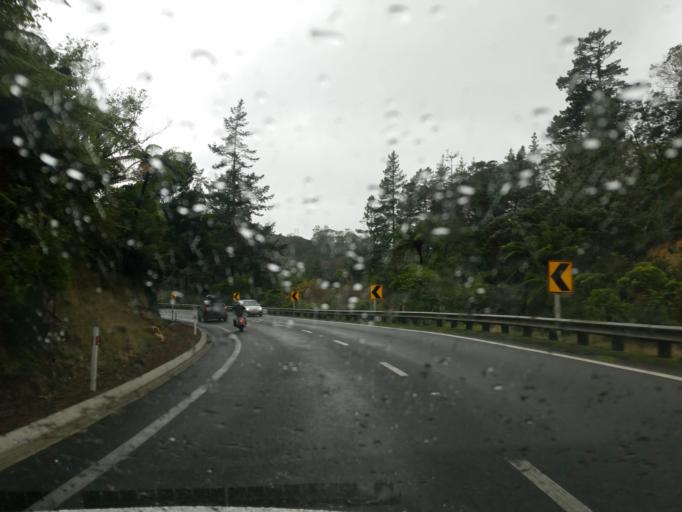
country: NZ
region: Waikato
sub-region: Hauraki District
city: Paeroa
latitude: -37.4202
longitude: 175.7352
